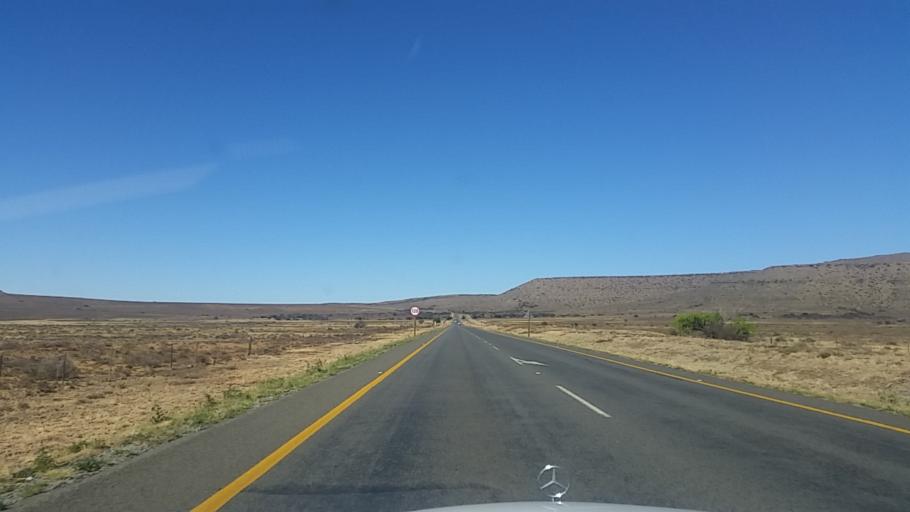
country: ZA
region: Eastern Cape
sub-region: Cacadu District Municipality
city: Graaff-Reinet
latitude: -31.9326
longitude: 24.7417
